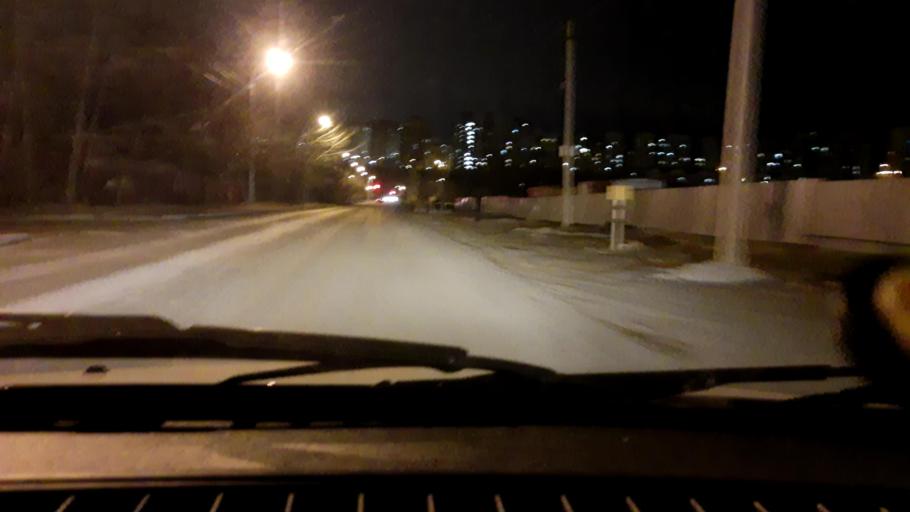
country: RU
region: Bashkortostan
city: Ufa
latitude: 54.6858
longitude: 55.9859
